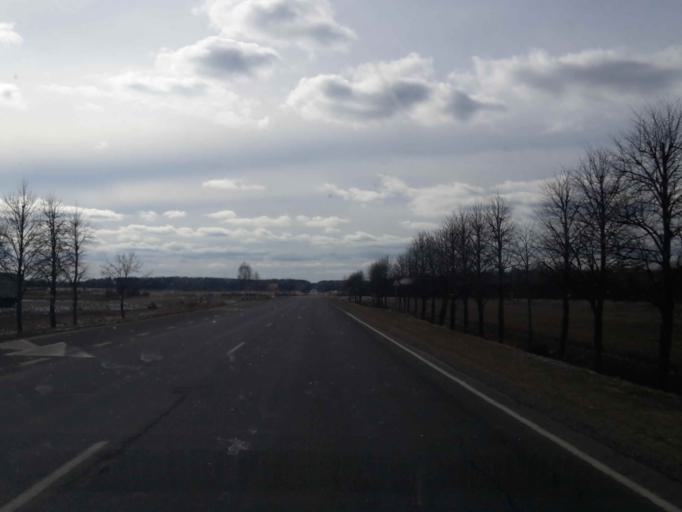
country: BY
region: Minsk
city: Myadzyel
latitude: 55.0585
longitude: 27.1361
